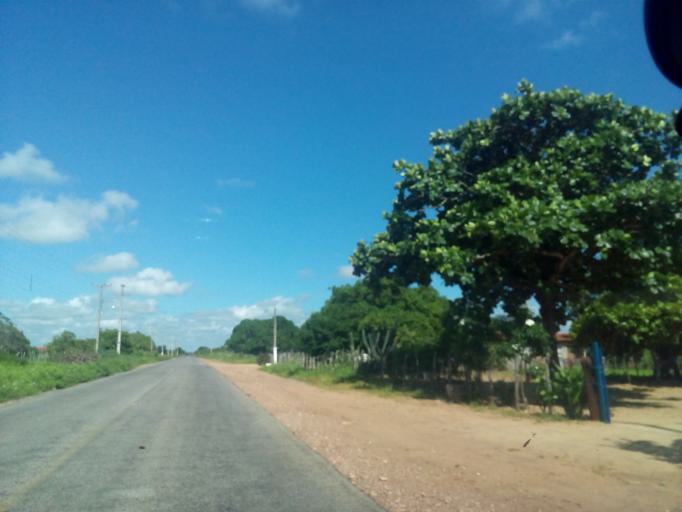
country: BR
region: Rio Grande do Norte
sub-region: Sao Paulo Do Potengi
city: Sao Paulo do Potengi
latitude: -5.9155
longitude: -35.7120
